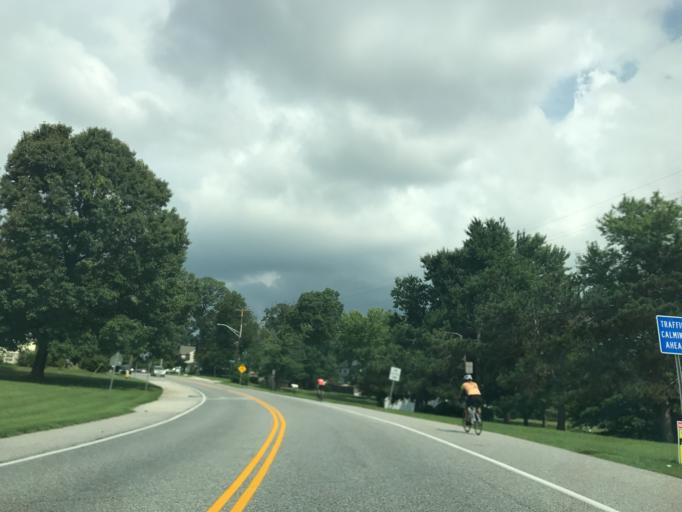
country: US
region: Maryland
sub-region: Anne Arundel County
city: South Gate
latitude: 39.1258
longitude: -76.6444
